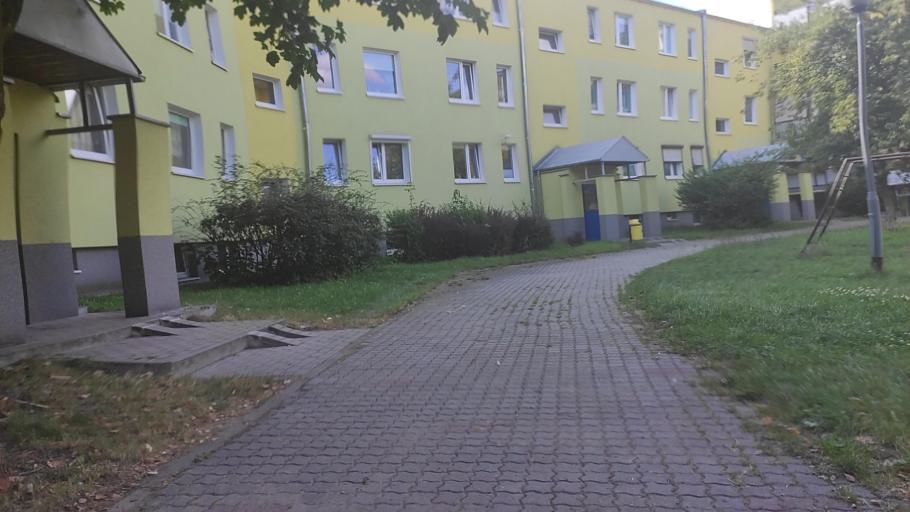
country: PL
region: Greater Poland Voivodeship
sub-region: Powiat poznanski
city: Swarzedz
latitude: 52.3996
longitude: 17.0604
